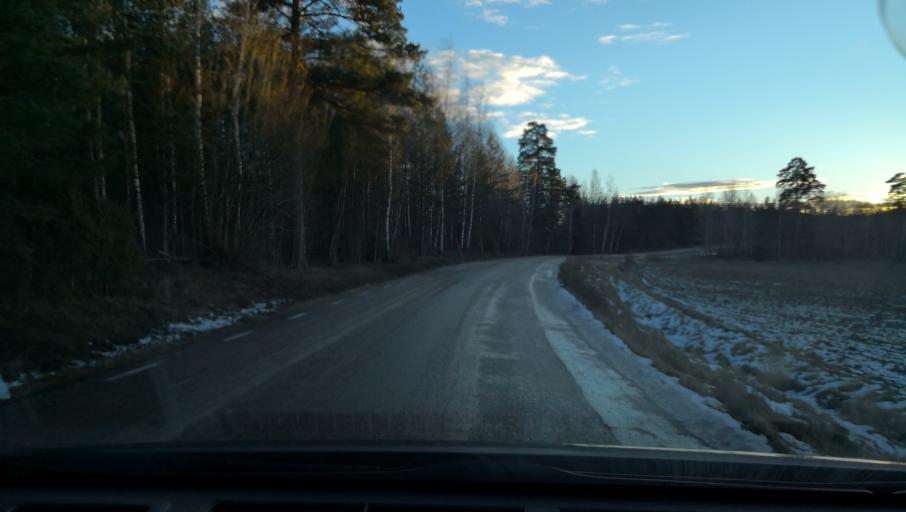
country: SE
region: Vaestmanland
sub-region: Vasteras
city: Tillberga
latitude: 59.7772
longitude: 16.6103
